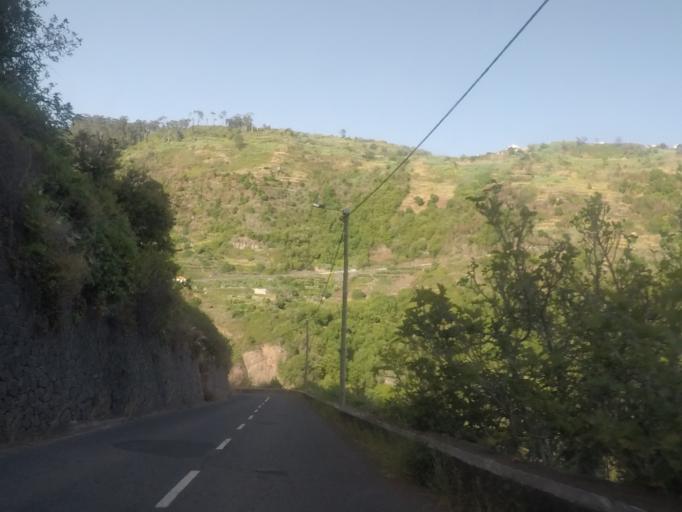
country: PT
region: Madeira
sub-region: Calheta
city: Arco da Calheta
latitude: 32.7102
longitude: -17.1355
